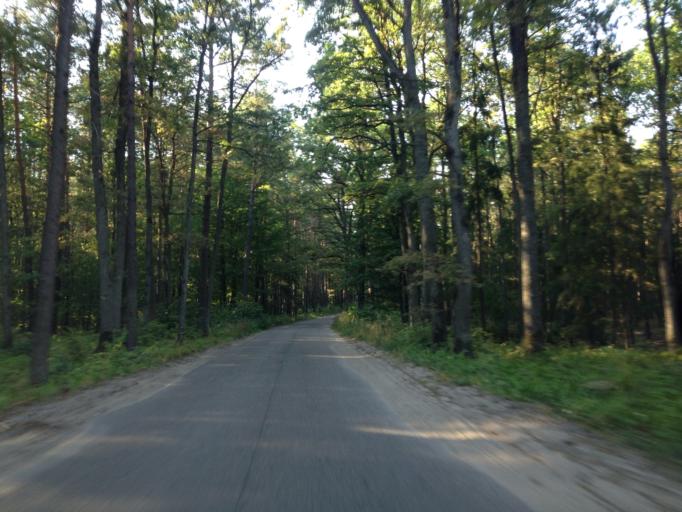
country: PL
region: Warmian-Masurian Voivodeship
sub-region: Powiat dzialdowski
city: Lidzbark
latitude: 53.2433
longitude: 19.7487
